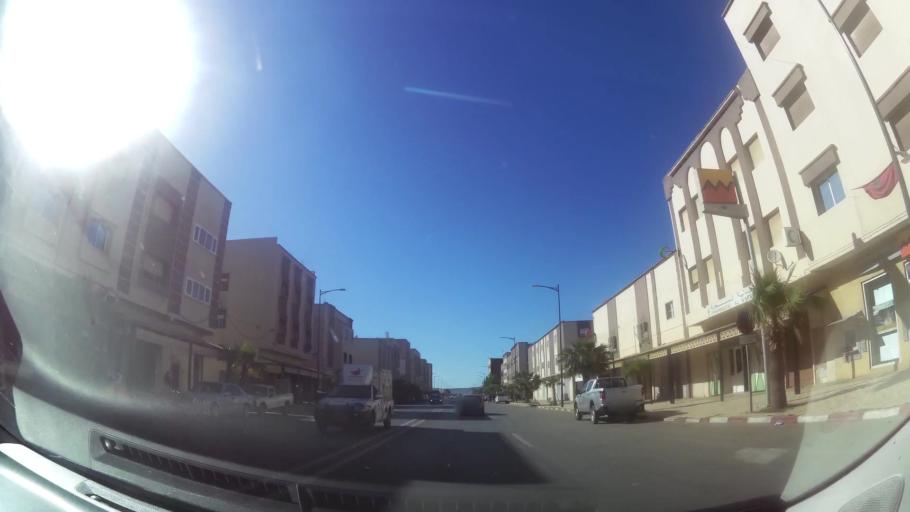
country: MA
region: Oriental
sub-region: Berkane-Taourirt
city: Ahfir
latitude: 34.8609
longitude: -1.9949
